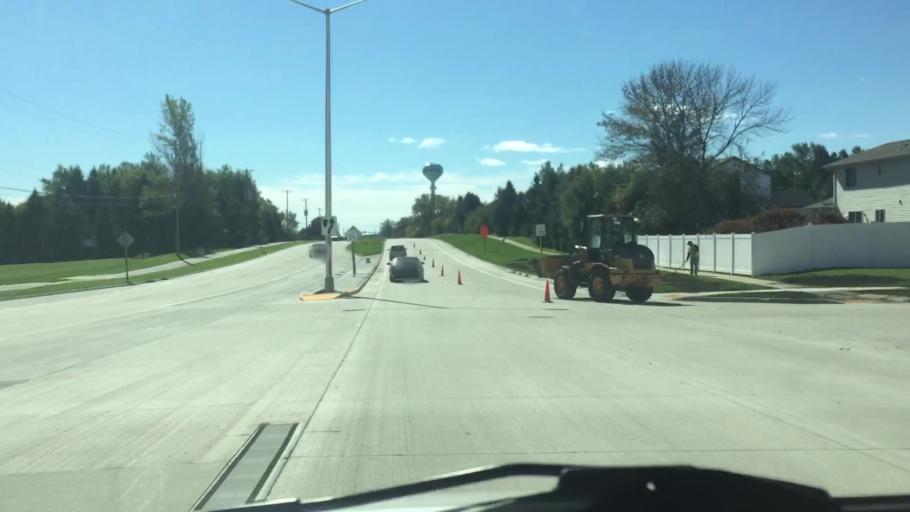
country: US
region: Wisconsin
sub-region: Waukesha County
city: Pewaukee
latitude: 43.0430
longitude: -88.2859
